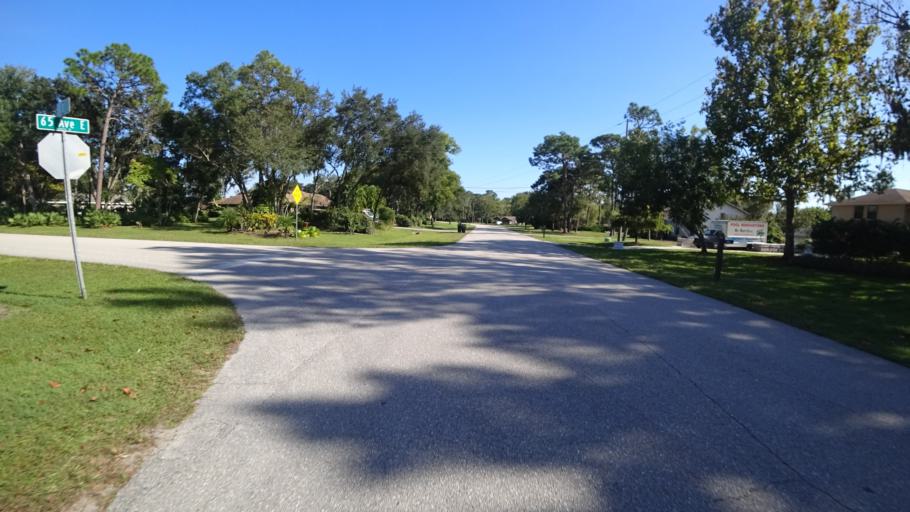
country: US
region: Florida
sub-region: Sarasota County
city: The Meadows
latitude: 27.4234
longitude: -82.4459
